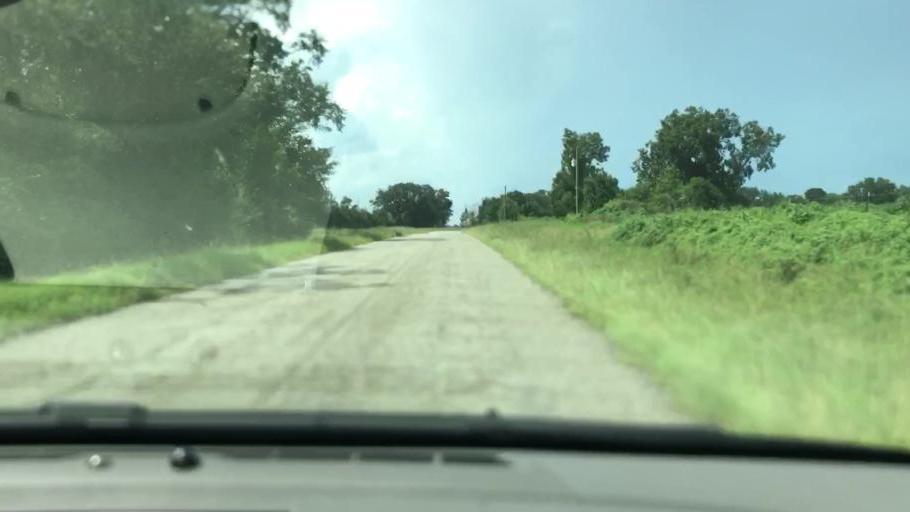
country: US
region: Georgia
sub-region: Seminole County
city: Donalsonville
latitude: 31.1640
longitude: -85.0000
